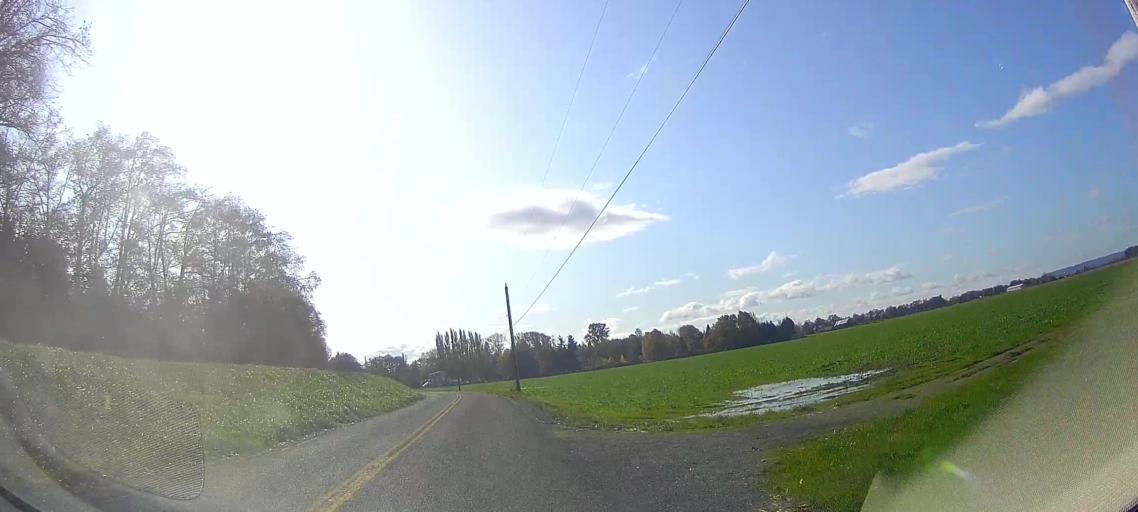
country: US
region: Washington
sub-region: Skagit County
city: Mount Vernon
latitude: 48.3324
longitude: -122.3523
